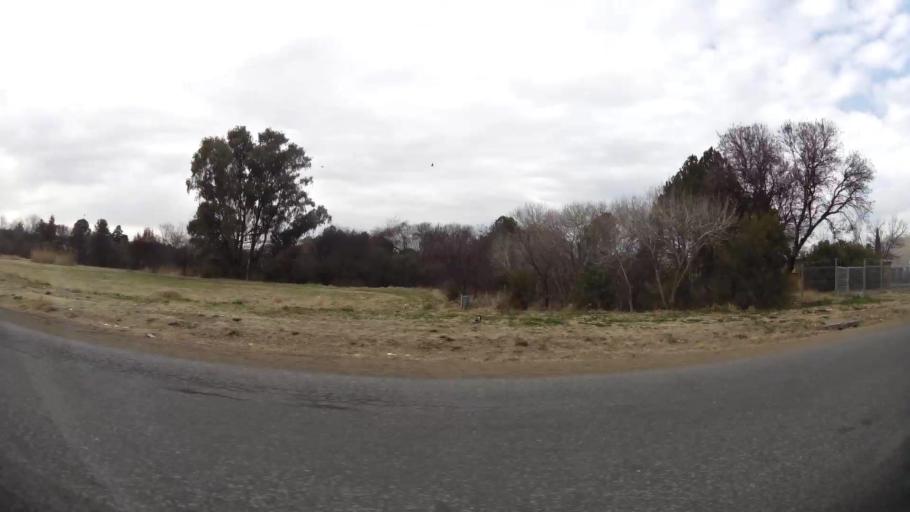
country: ZA
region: Orange Free State
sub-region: Fezile Dabi District Municipality
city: Kroonstad
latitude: -27.6453
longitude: 27.2387
